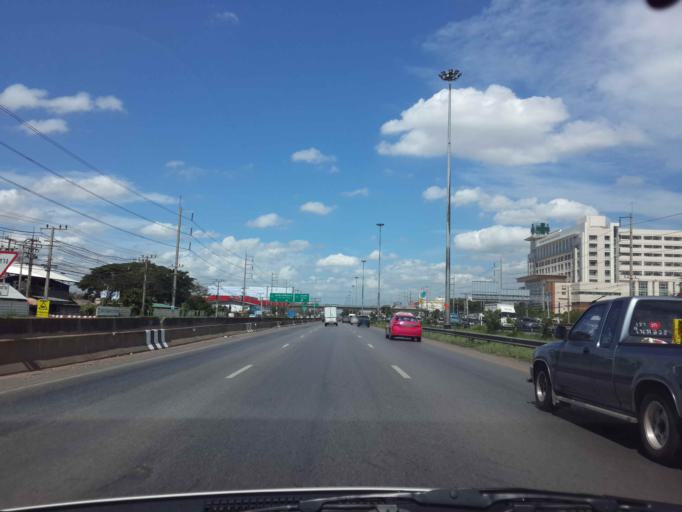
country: TH
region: Samut Sakhon
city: Samut Sakhon
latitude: 13.5387
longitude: 100.2266
